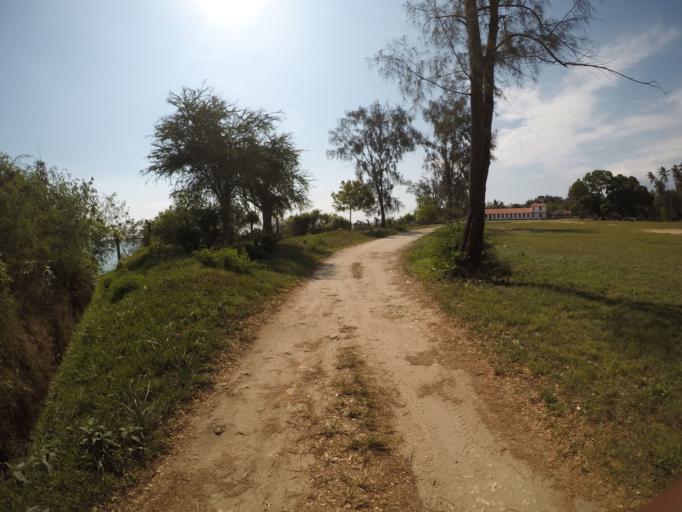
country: TZ
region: Zanzibar Urban/West
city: Zanzibar
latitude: -6.1219
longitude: 39.2131
